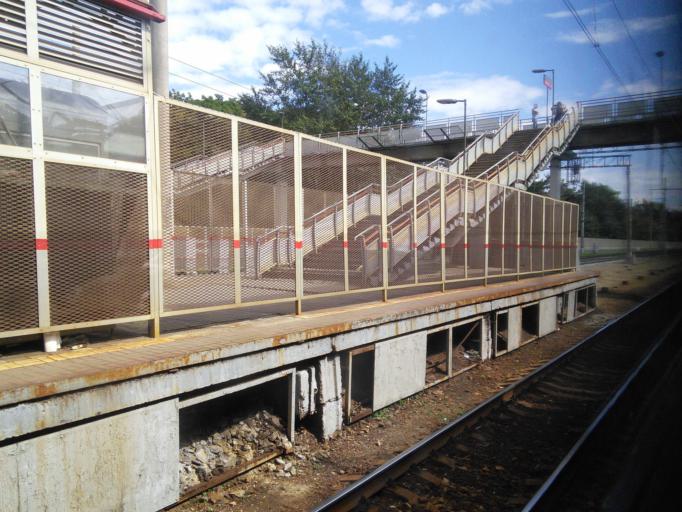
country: RU
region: Moscow
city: Zhulebino
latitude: 55.6984
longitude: 37.8648
